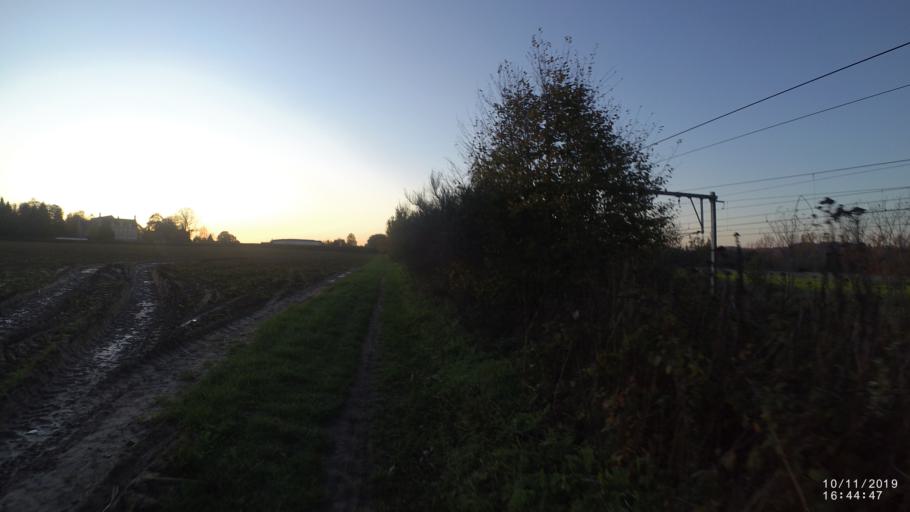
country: BE
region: Flanders
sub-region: Provincie Vlaams-Brabant
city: Bierbeek
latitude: 50.8559
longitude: 4.7543
